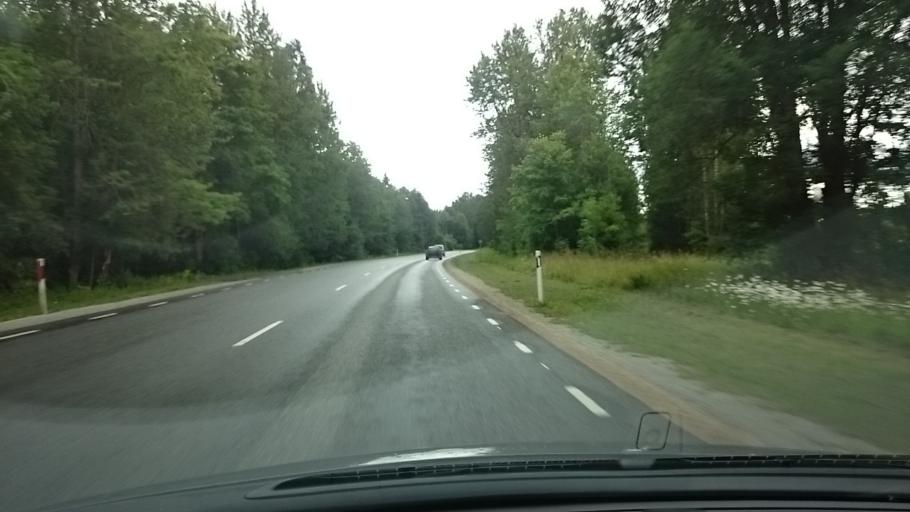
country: EE
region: Harju
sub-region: Keila linn
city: Keila
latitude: 59.2623
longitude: 24.2913
